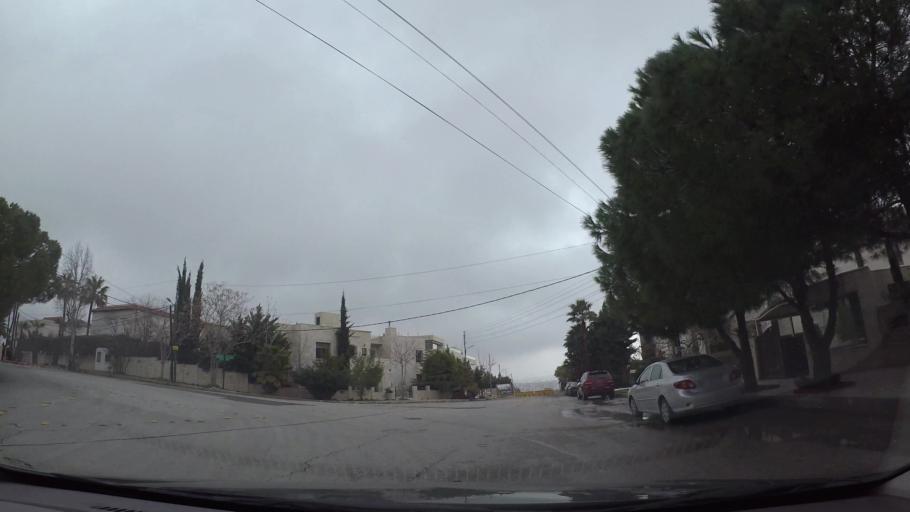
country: JO
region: Amman
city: Al Bunayyat ash Shamaliyah
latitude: 31.9367
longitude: 35.8813
